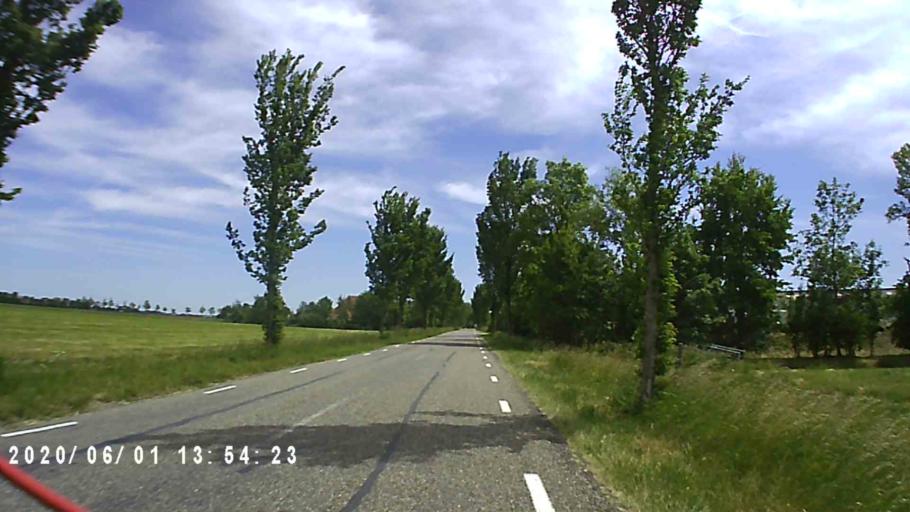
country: NL
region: Friesland
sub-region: Gemeente Littenseradiel
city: Makkum
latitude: 53.1037
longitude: 5.6354
